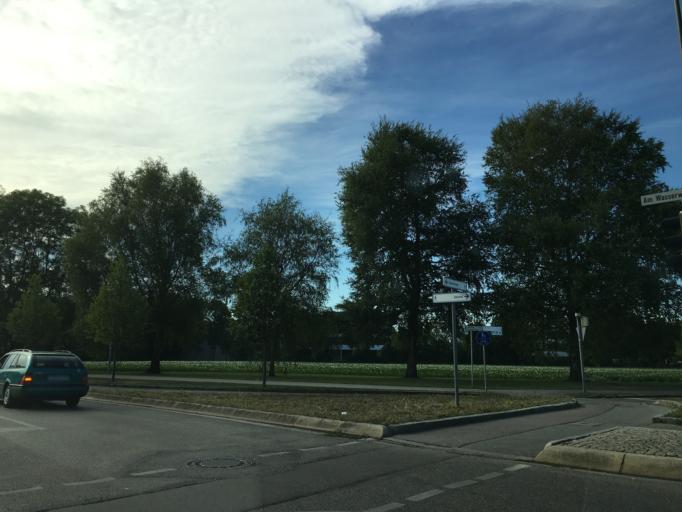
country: DE
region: Bavaria
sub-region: Upper Bavaria
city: Erding
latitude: 48.2931
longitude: 11.8998
